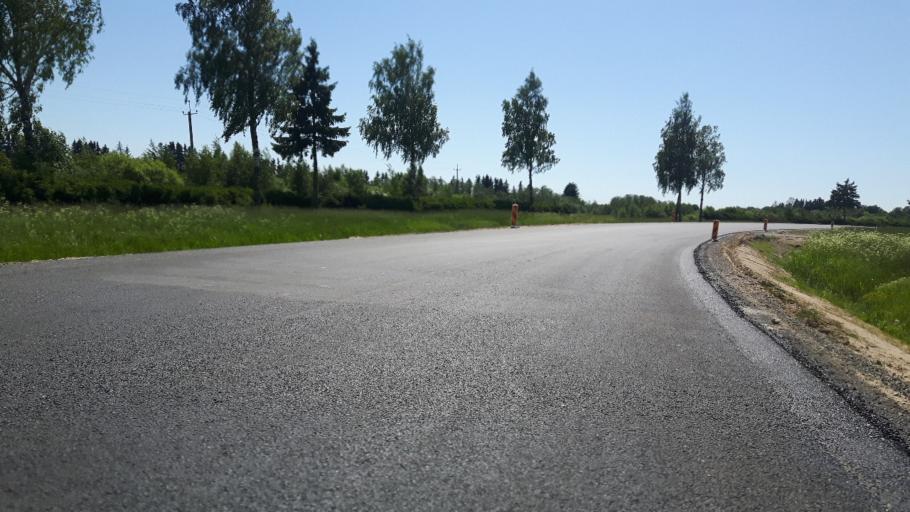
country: EE
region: Paernumaa
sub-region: Sindi linn
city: Sindi
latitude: 58.4248
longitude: 24.7242
